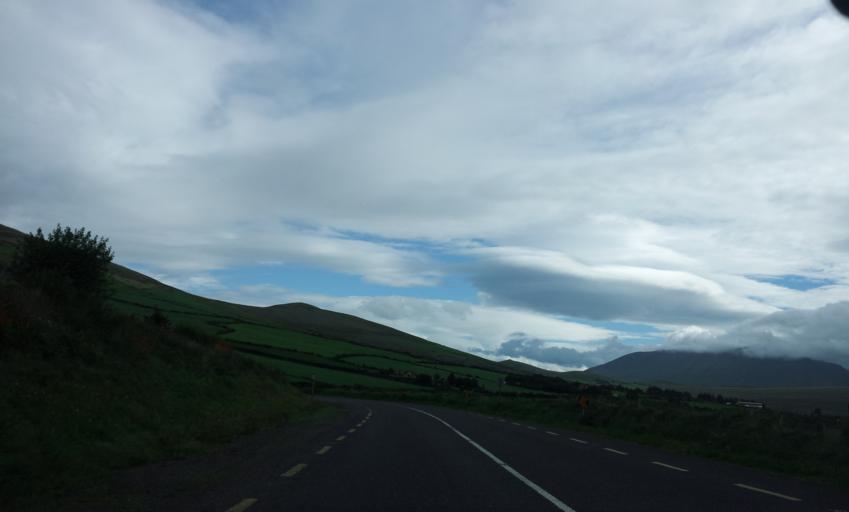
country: IE
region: Munster
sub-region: Ciarrai
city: Killorglin
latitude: 52.1747
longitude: -9.9904
